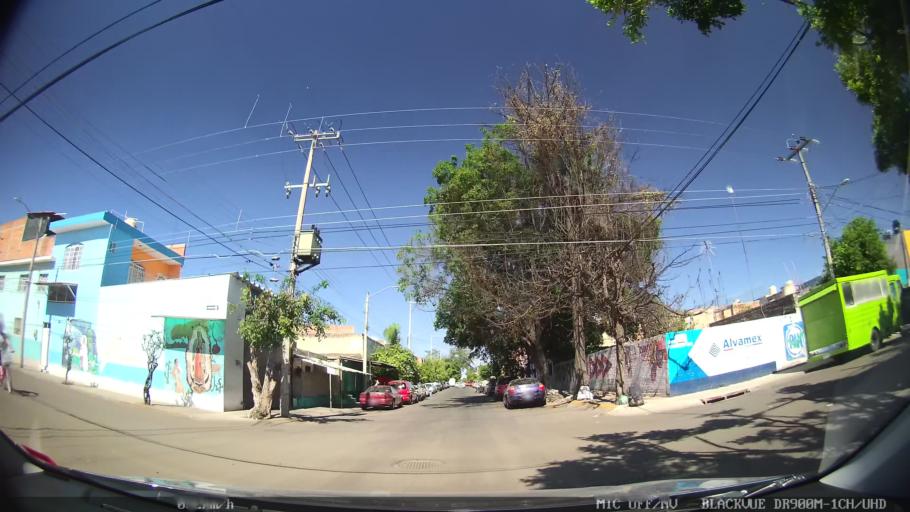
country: MX
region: Jalisco
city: Tlaquepaque
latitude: 20.6570
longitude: -103.2913
